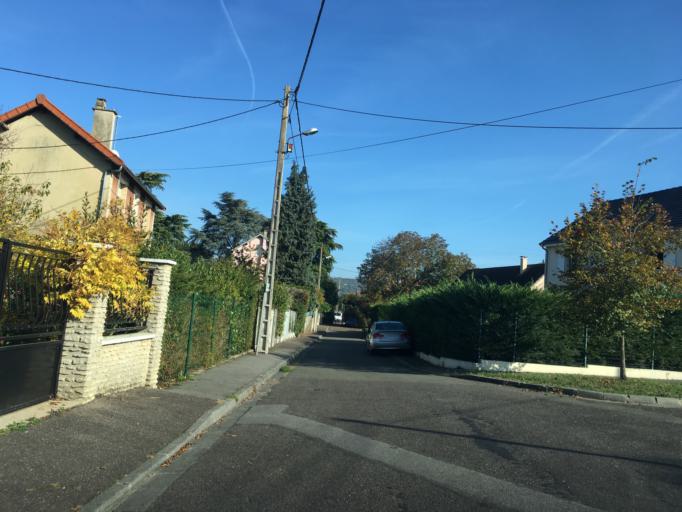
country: FR
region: Haute-Normandie
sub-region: Departement de l'Eure
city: Vernon
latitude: 49.0839
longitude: 1.4837
